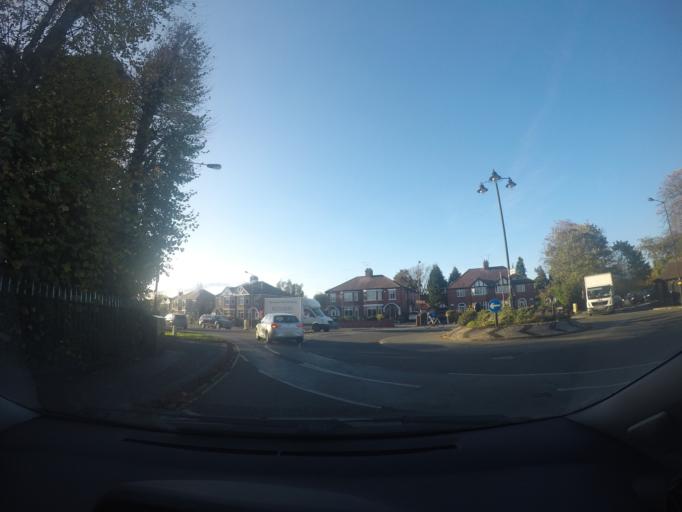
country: GB
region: England
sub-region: City of York
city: York
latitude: 53.9676
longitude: -1.0631
